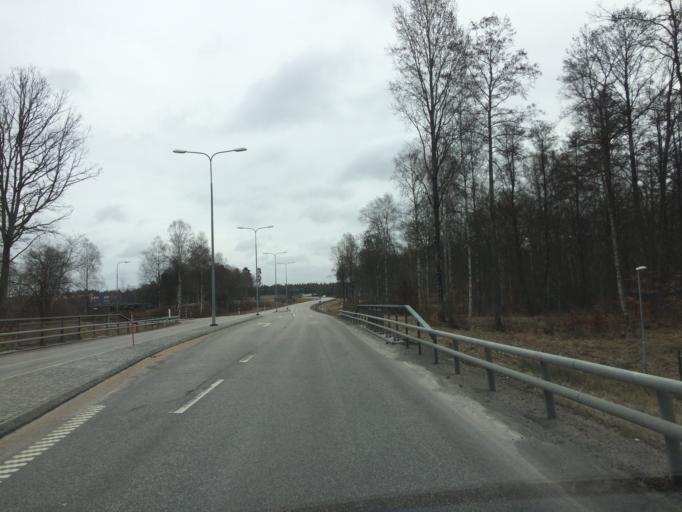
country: SE
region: Kronoberg
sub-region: Almhults Kommun
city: AElmhult
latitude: 56.5490
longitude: 14.1479
